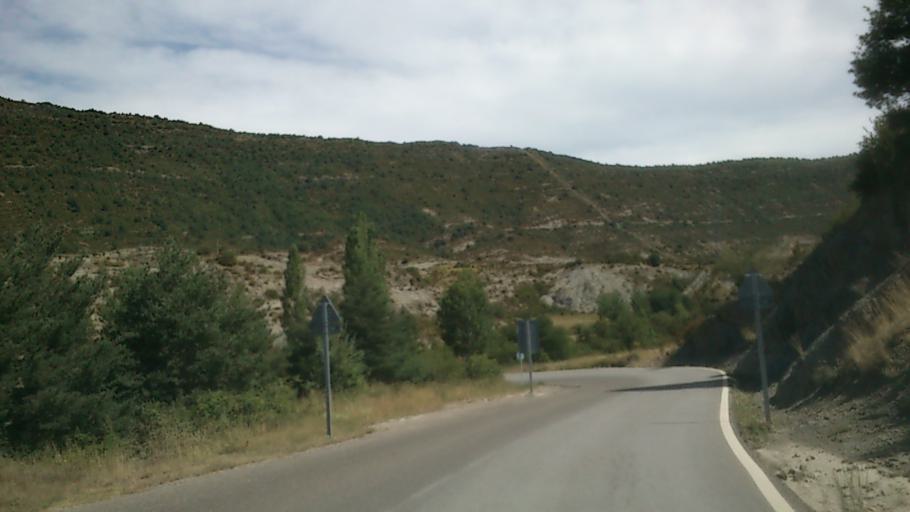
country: ES
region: Aragon
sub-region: Provincia de Huesca
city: Arguis
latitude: 42.3142
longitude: -0.4301
